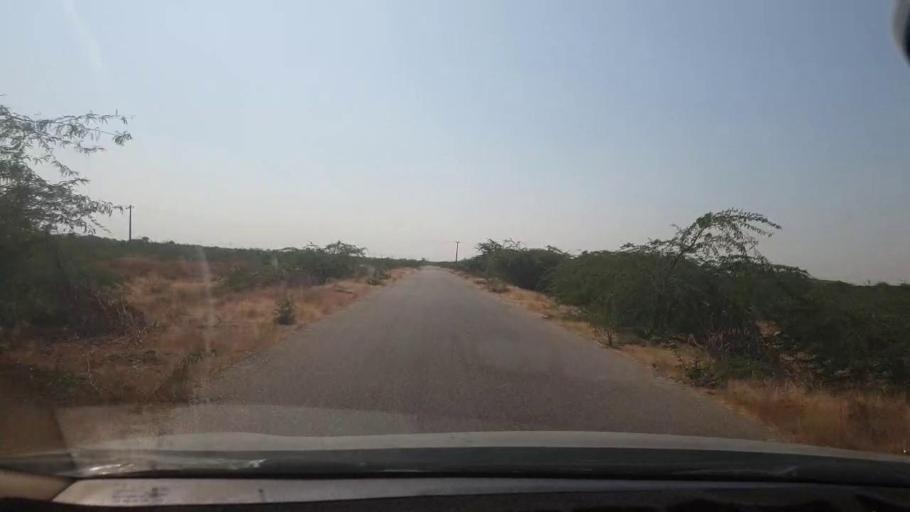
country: PK
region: Sindh
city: Malir Cantonment
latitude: 25.1619
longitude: 67.1516
